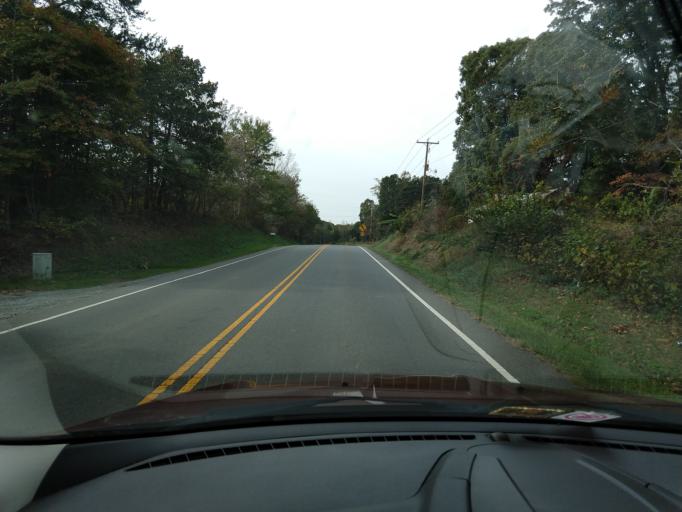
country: US
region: Virginia
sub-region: Franklin County
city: Union Hall
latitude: 36.9977
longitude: -79.6999
